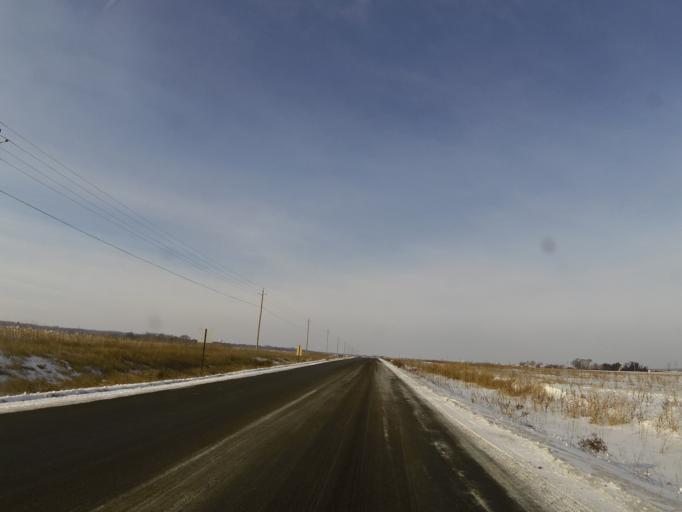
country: US
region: Minnesota
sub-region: Scott County
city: Prior Lake
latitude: 44.7682
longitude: -93.4612
